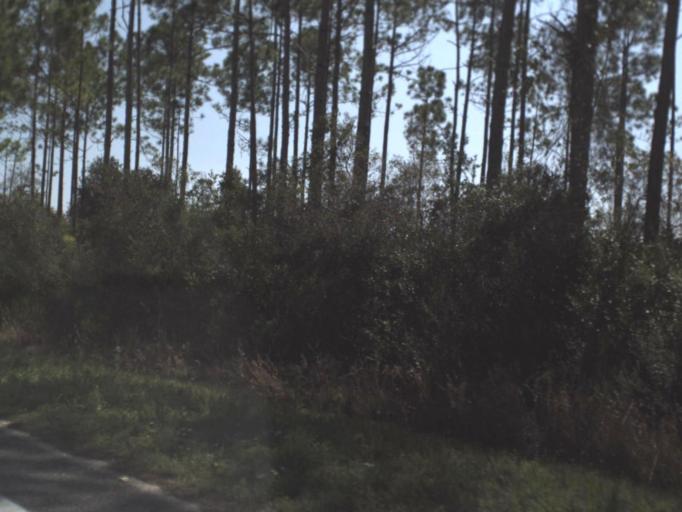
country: US
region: Florida
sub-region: Gulf County
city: Port Saint Joe
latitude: 29.7576
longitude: -85.2565
